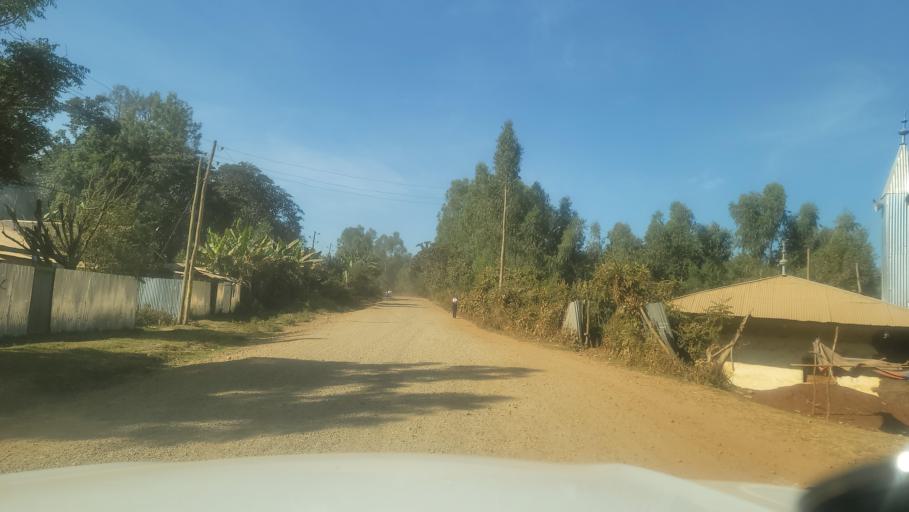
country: ET
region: Oromiya
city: Agaro
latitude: 7.8393
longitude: 36.5440
